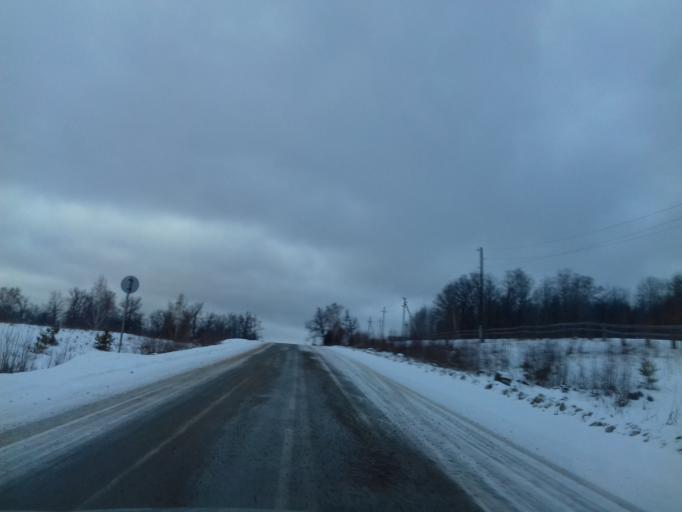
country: RU
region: Bashkortostan
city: Starosubkhangulovo
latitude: 53.2281
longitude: 57.4546
